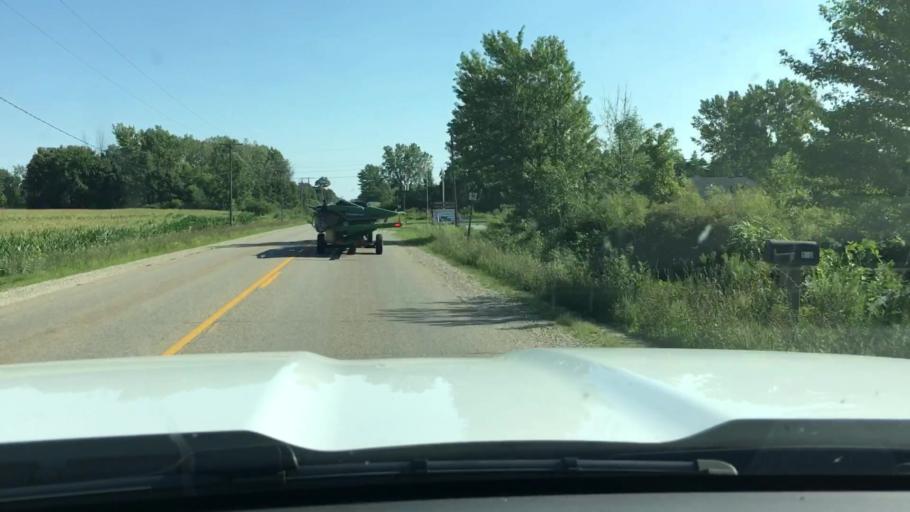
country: US
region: Michigan
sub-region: Ottawa County
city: Coopersville
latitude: 43.0702
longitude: -85.9569
